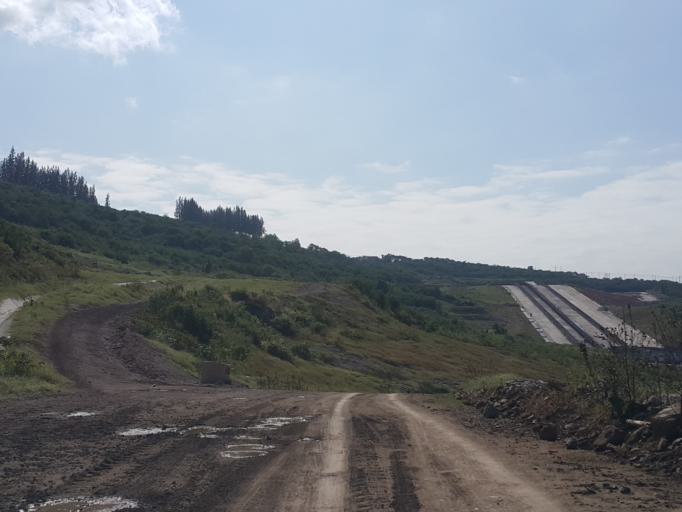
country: TH
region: Lampang
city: Mae Mo
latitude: 18.3237
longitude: 99.7378
